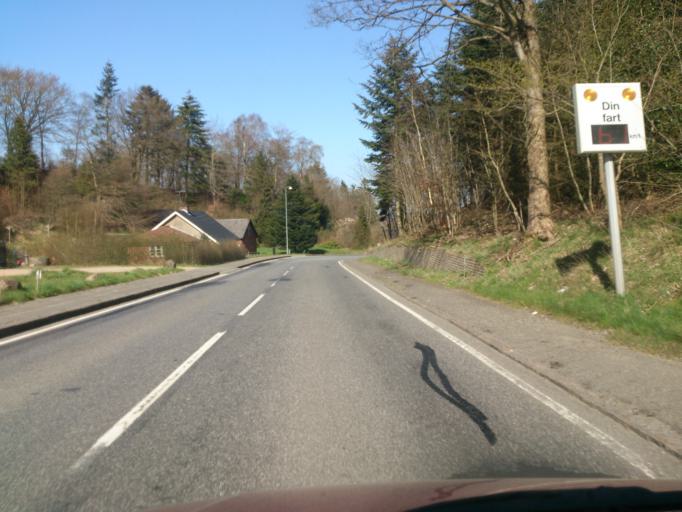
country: DK
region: Central Jutland
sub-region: Viborg Kommune
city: Bjerringbro
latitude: 56.4479
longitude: 9.7169
